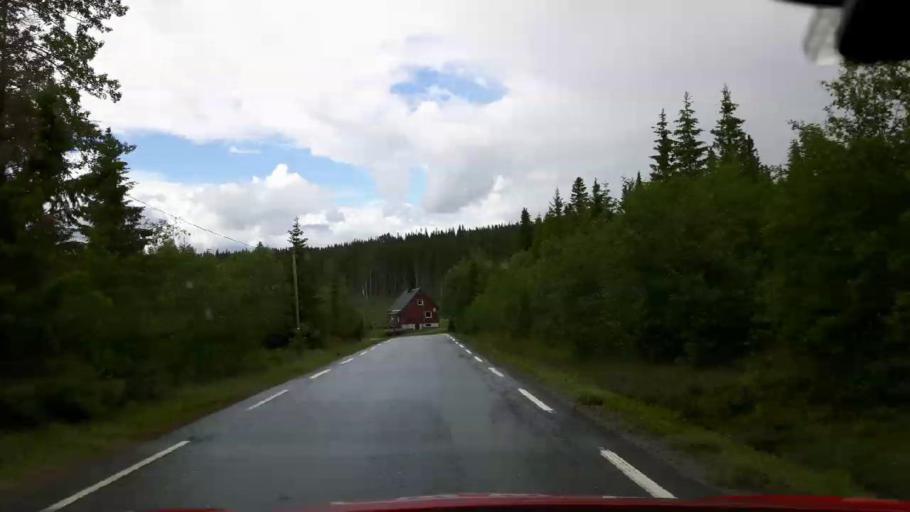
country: NO
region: Nord-Trondelag
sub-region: Lierne
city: Sandvika
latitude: 64.1014
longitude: 14.0239
